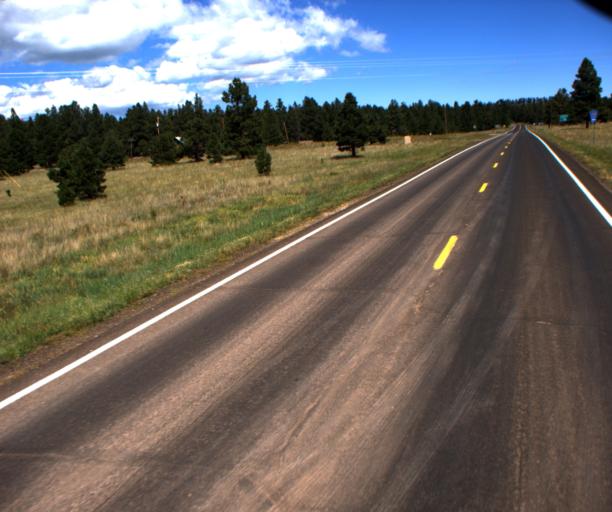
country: US
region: Arizona
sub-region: Apache County
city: Eagar
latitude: 34.0293
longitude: -109.4509
